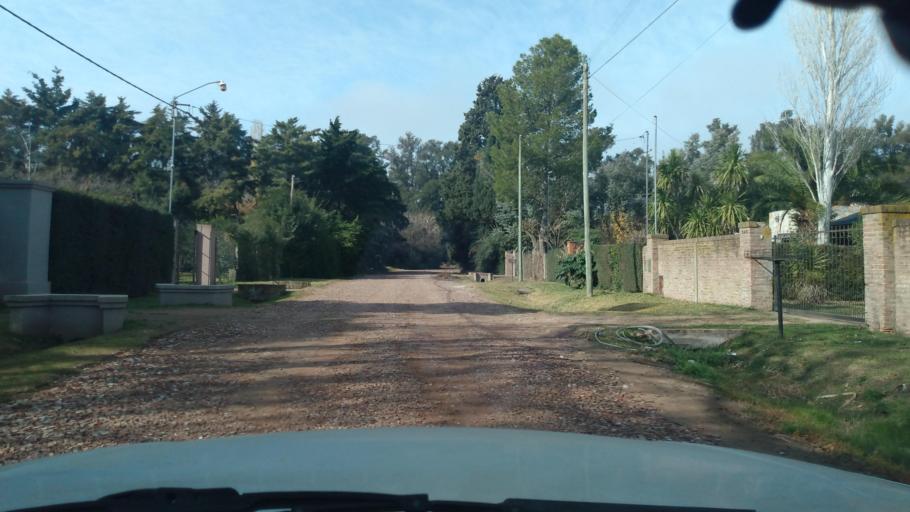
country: AR
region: Buenos Aires
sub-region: Partido de Lujan
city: Lujan
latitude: -34.5934
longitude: -59.1382
